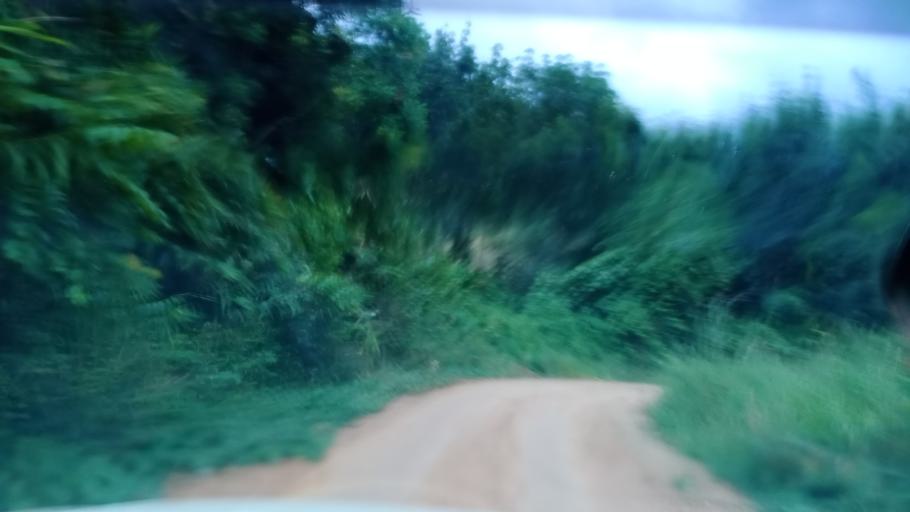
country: TH
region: Changwat Bueng Kan
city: Pak Khat
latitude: 18.7270
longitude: 103.2703
